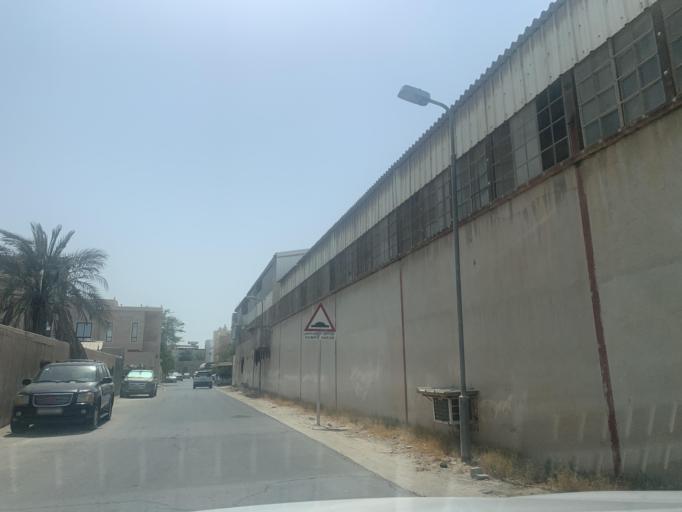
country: BH
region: Manama
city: Jidd Hafs
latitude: 26.2199
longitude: 50.4700
